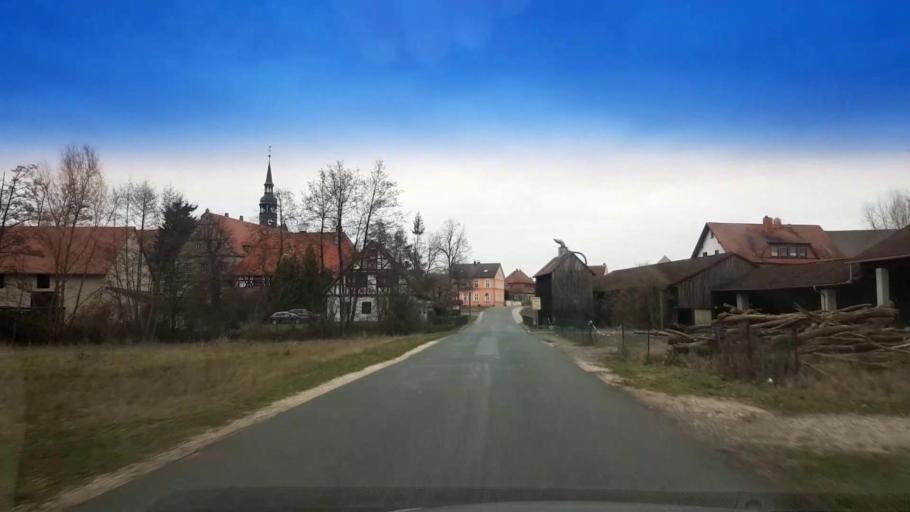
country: DE
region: Bavaria
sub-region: Upper Franconia
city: Pettstadt
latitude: 49.7916
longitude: 10.9074
